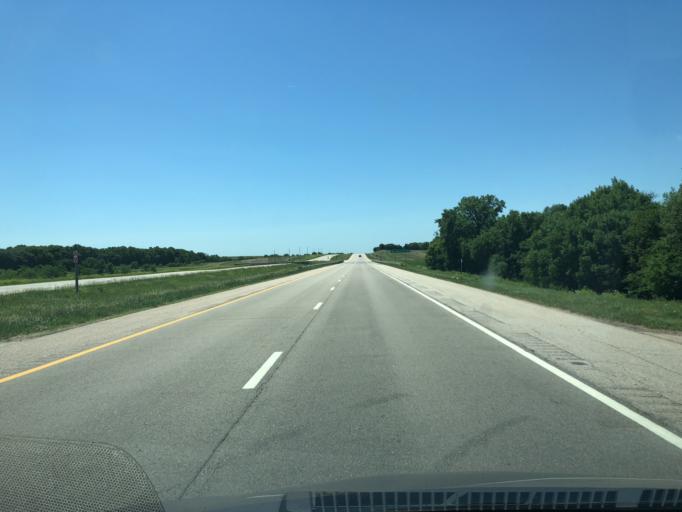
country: US
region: Kansas
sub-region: Republic County
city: Belleville
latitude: 39.9600
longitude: -97.6136
